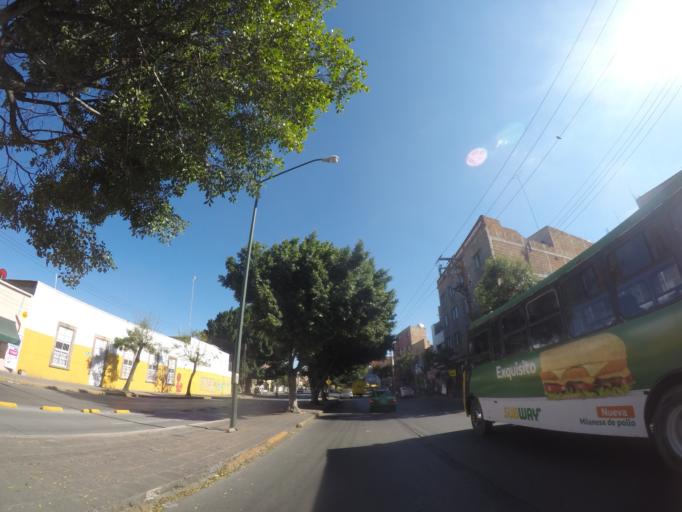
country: MX
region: San Luis Potosi
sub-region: San Luis Potosi
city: San Luis Potosi
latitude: 22.1570
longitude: -100.9746
